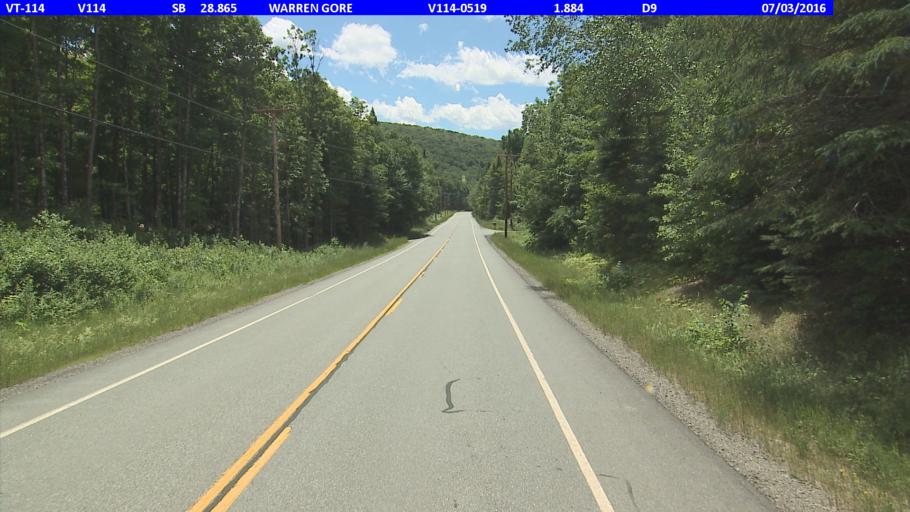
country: CA
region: Quebec
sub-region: Estrie
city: Coaticook
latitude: 44.9109
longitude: -71.8757
